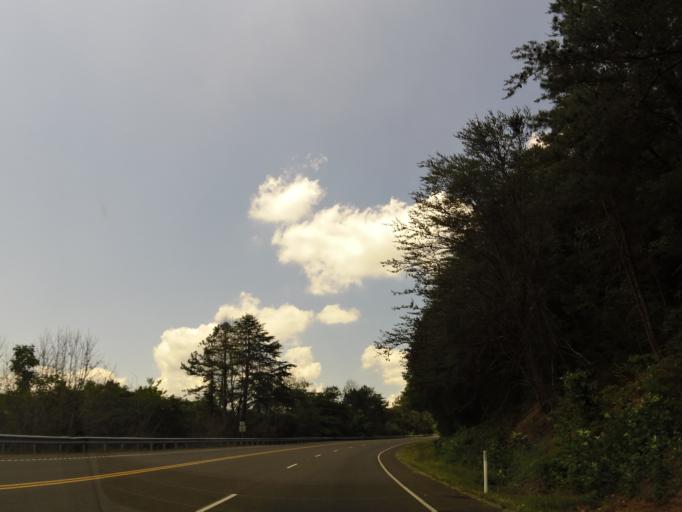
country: US
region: Tennessee
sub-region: Rhea County
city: Dayton
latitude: 35.5039
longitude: -85.0409
